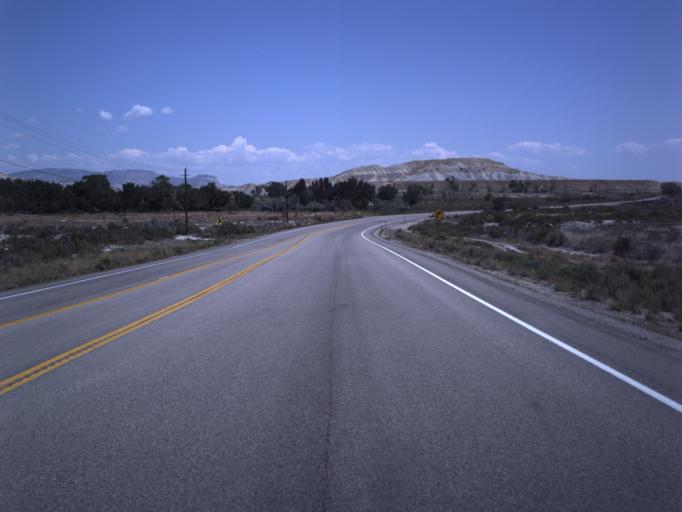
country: US
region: Utah
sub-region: Emery County
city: Ferron
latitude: 39.1131
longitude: -111.1250
